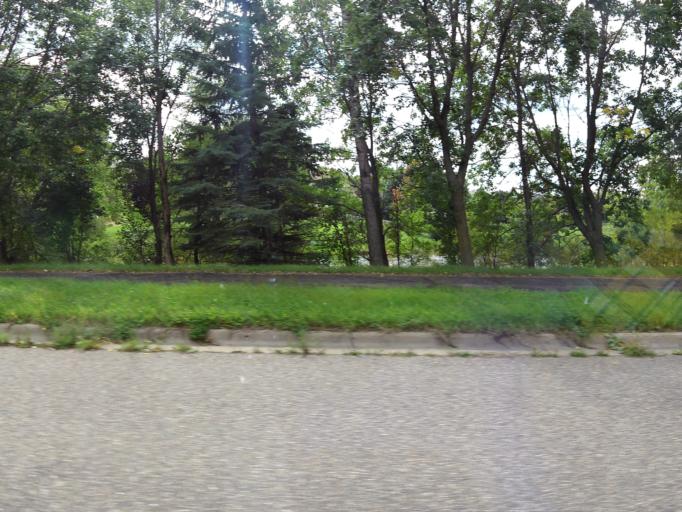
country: US
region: Minnesota
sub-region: Dakota County
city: Apple Valley
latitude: 44.7173
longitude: -93.2478
